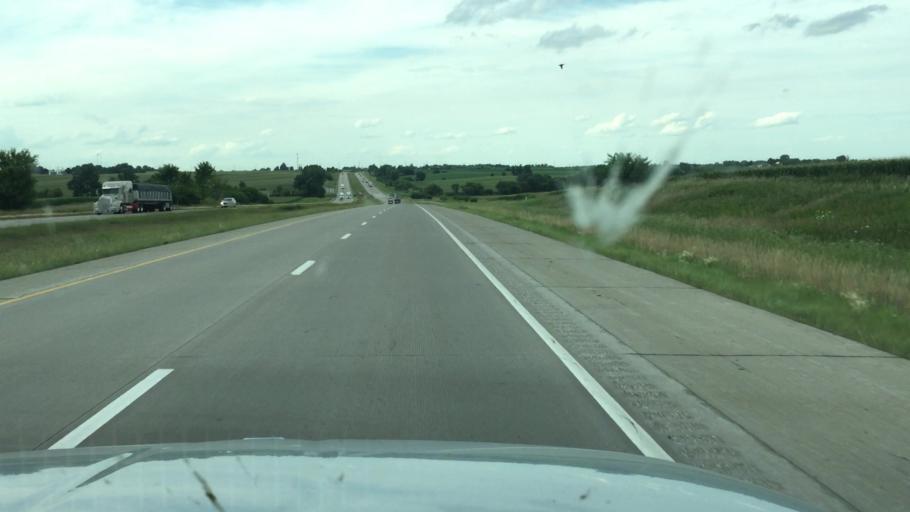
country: US
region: Iowa
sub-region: Scott County
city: Blue Grass
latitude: 41.5491
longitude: -90.6779
